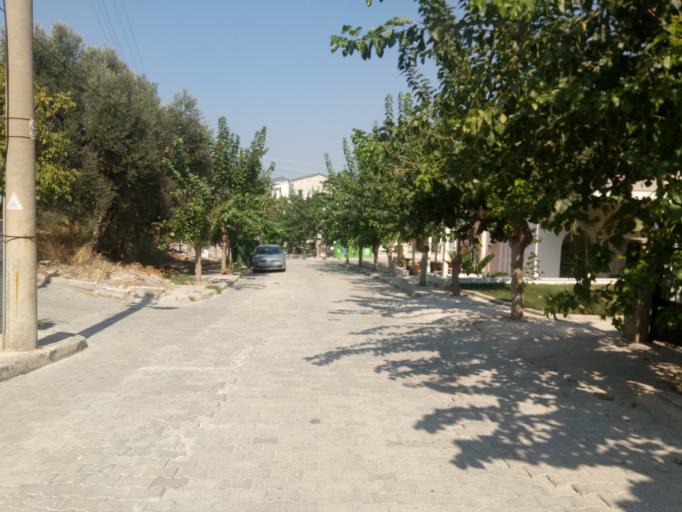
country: TR
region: Izmir
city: Urla
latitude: 38.3268
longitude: 26.7694
